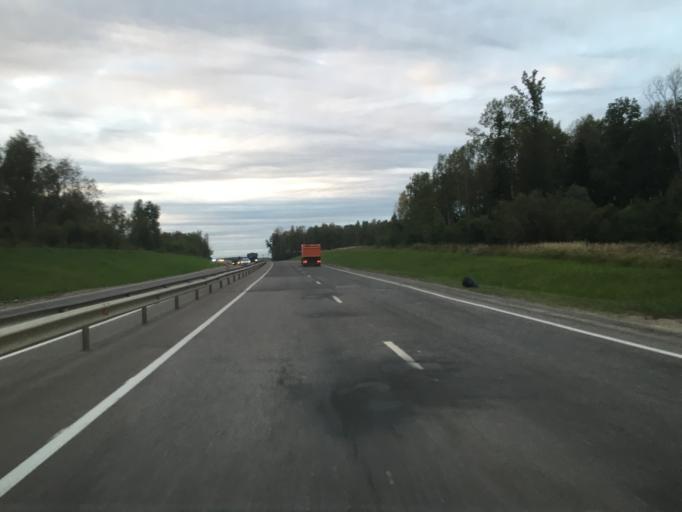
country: RU
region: Kaluga
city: Kaluga
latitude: 54.6088
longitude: 36.3107
